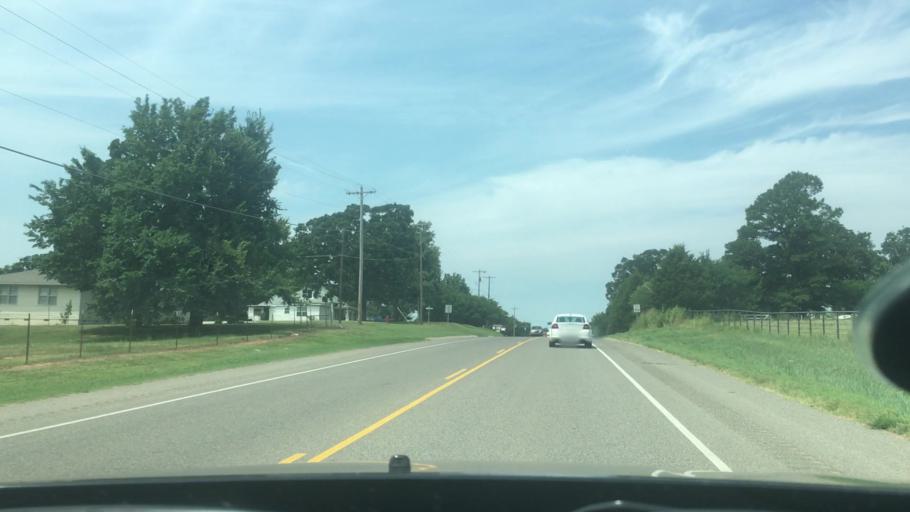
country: US
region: Oklahoma
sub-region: Pottawatomie County
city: Shawnee
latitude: 35.3332
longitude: -96.8489
